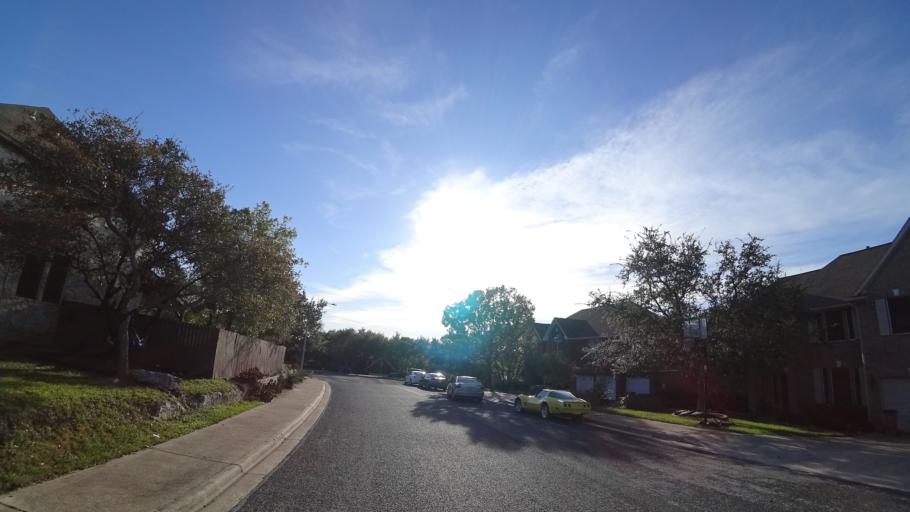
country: US
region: Texas
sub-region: Williamson County
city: Jollyville
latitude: 30.4024
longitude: -97.7696
